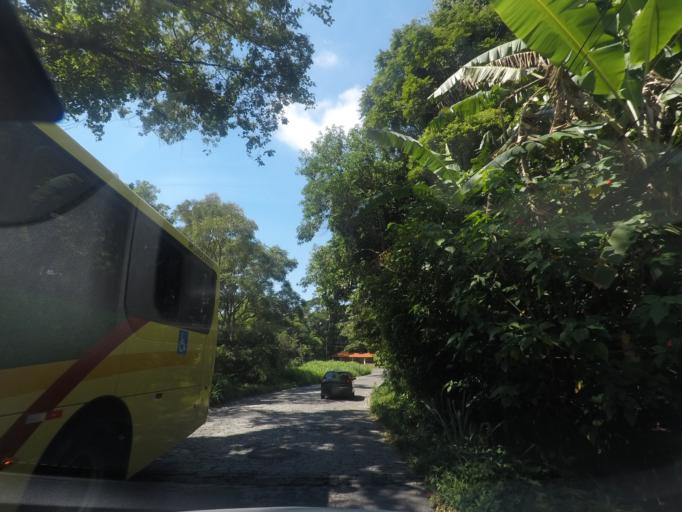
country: BR
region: Rio de Janeiro
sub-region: Petropolis
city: Petropolis
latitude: -22.5471
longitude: -43.1830
